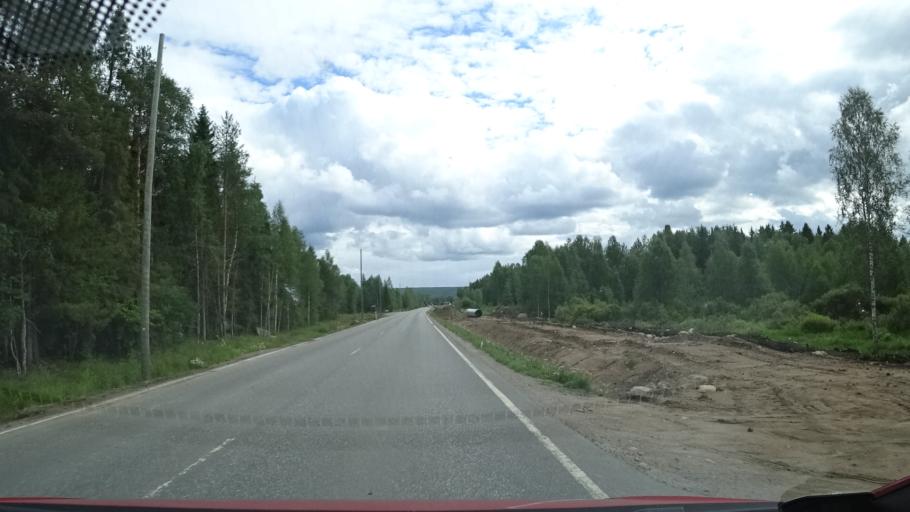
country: FI
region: Lapland
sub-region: Rovaniemi
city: Rovaniemi
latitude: 66.5309
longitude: 25.7366
